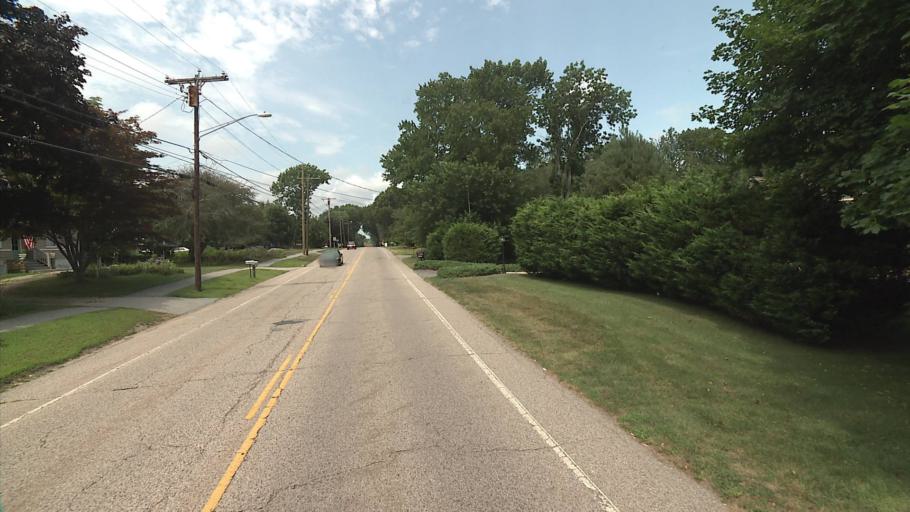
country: US
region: Connecticut
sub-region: New London County
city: Central Waterford
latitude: 41.3258
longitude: -72.1343
